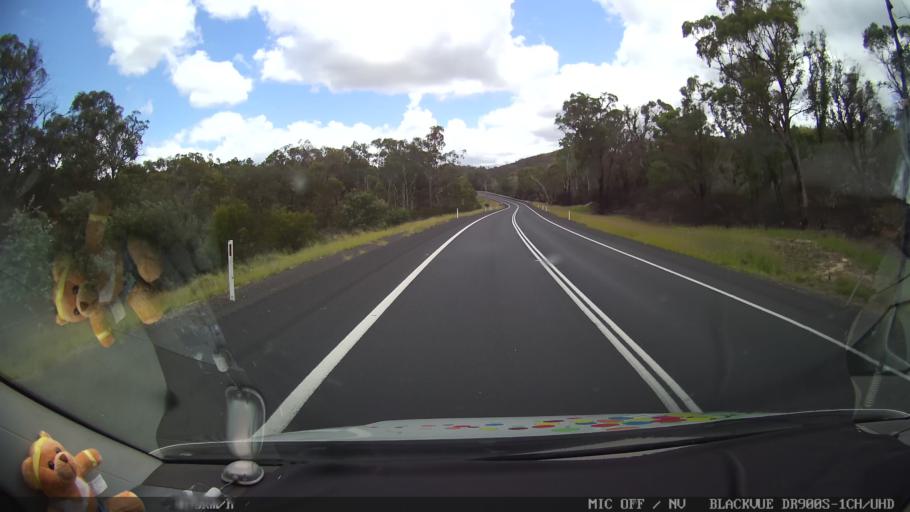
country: AU
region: New South Wales
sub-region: Glen Innes Severn
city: Glen Innes
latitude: -29.3554
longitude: 151.8972
